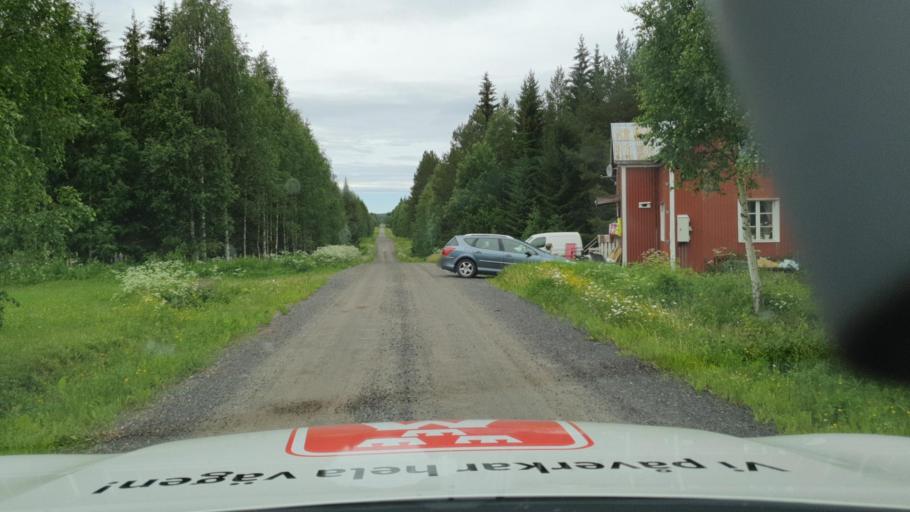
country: SE
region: Vaesterbotten
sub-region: Skelleftea Kommun
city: Burtraesk
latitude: 64.3944
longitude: 20.5892
